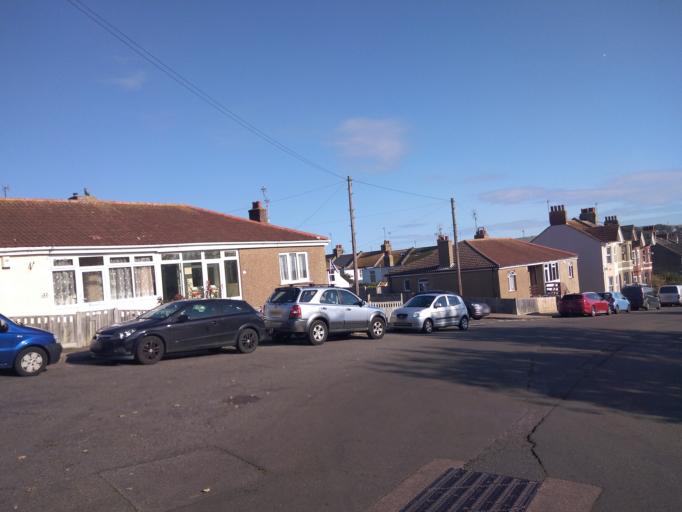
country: GB
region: England
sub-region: East Sussex
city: Newhaven
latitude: 50.7910
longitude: 0.0485
